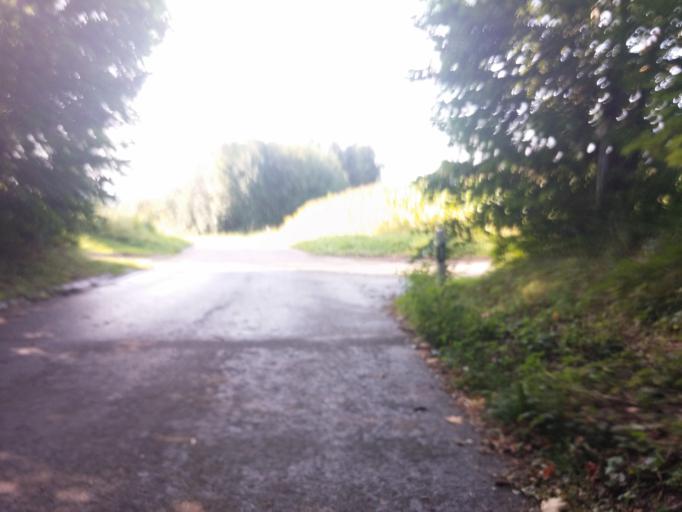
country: DE
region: Baden-Wuerttemberg
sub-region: Tuebingen Region
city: Aitrach
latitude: 47.9395
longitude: 10.1118
